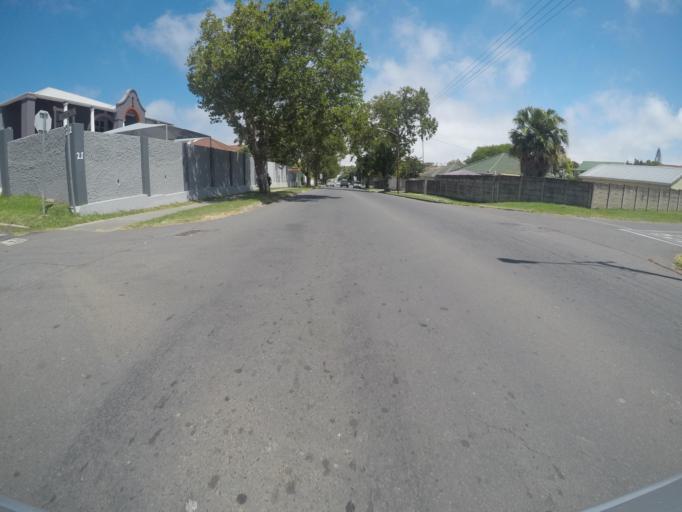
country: ZA
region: Eastern Cape
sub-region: Buffalo City Metropolitan Municipality
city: East London
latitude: -32.9867
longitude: 27.9019
